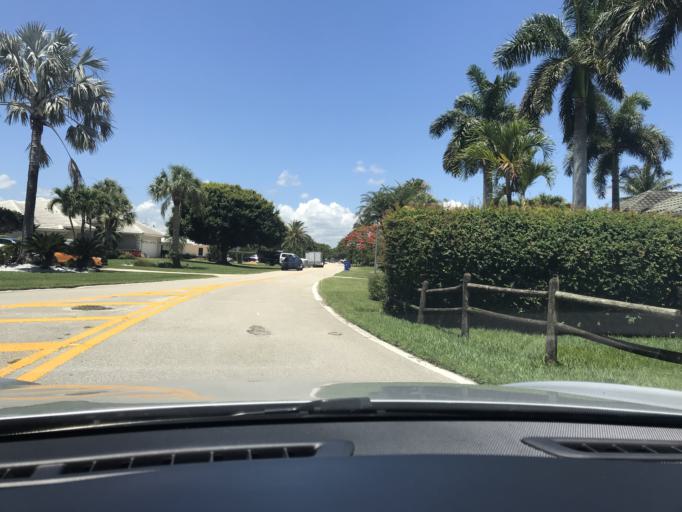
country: US
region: Florida
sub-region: Indian River County
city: Vero Beach
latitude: 27.6404
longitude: -80.3776
